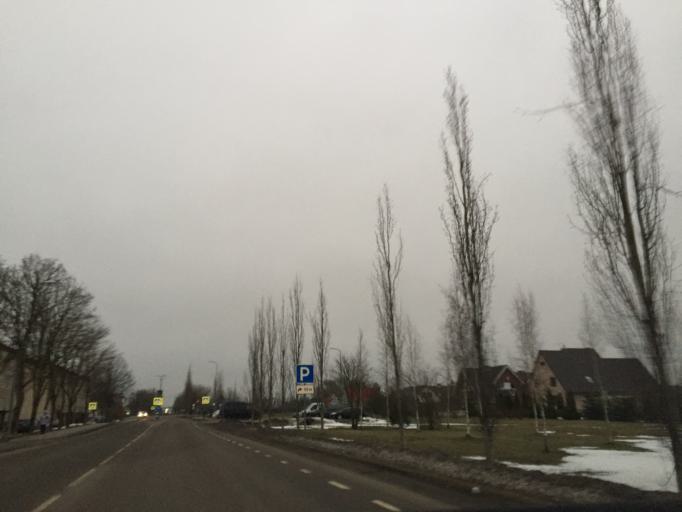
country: EE
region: Saare
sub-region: Kuressaare linn
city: Kuressaare
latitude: 58.2528
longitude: 22.5092
